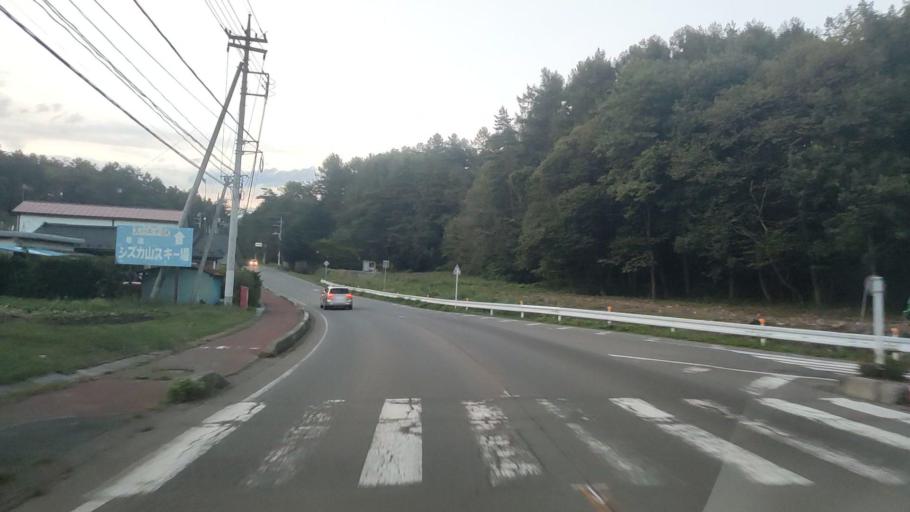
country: JP
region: Gunma
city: Nakanojomachi
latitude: 36.5160
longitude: 138.5993
